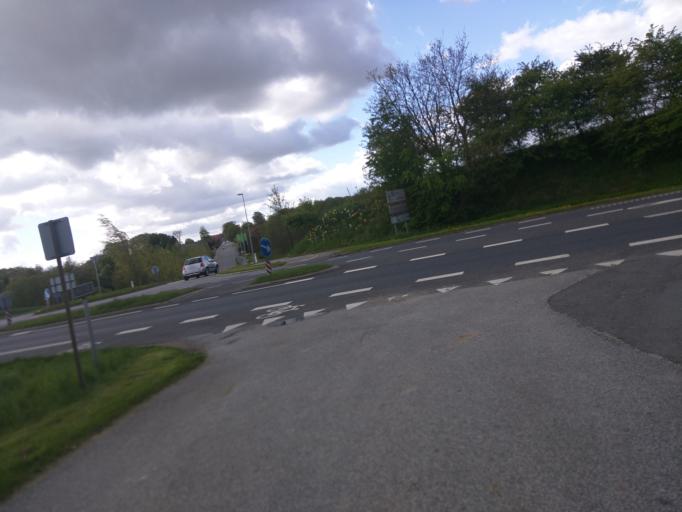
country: DK
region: Central Jutland
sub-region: Silkeborg Kommune
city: Kjellerup
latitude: 56.2971
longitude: 9.4267
